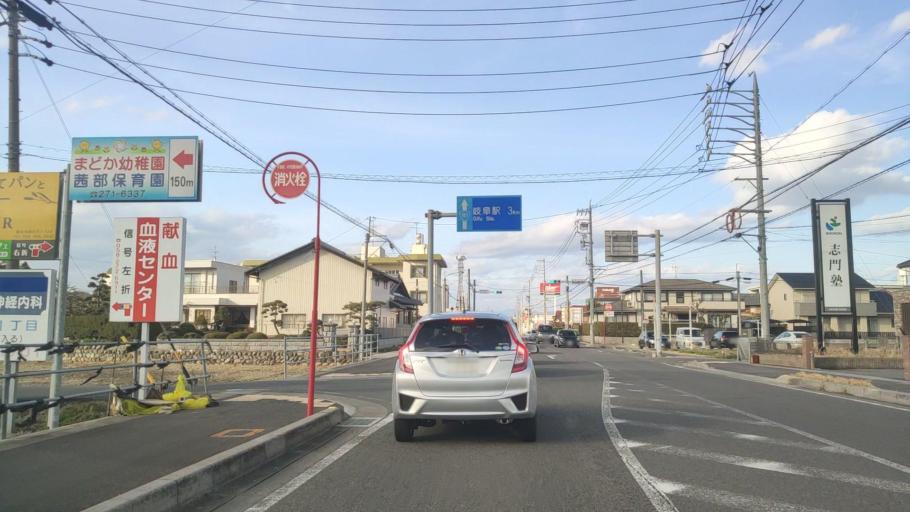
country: JP
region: Gifu
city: Kasamatsucho
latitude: 35.3893
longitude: 136.7546
